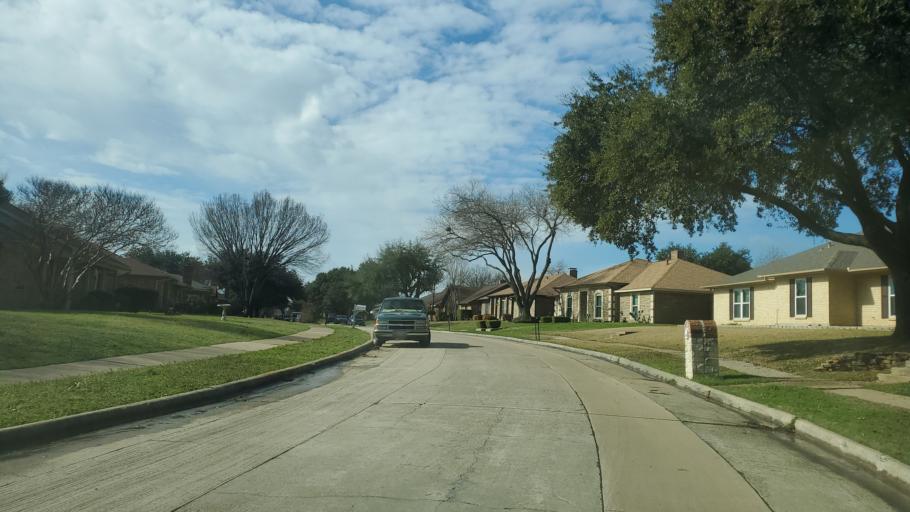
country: US
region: Texas
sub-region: Dallas County
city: Carrollton
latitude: 32.9794
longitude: -96.8789
